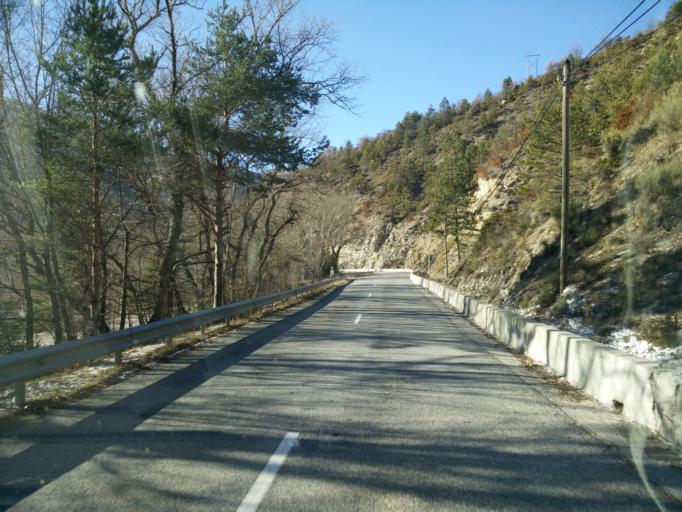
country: FR
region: Provence-Alpes-Cote d'Azur
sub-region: Departement des Alpes-de-Haute-Provence
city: Castellane
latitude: 43.8332
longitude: 6.4370
